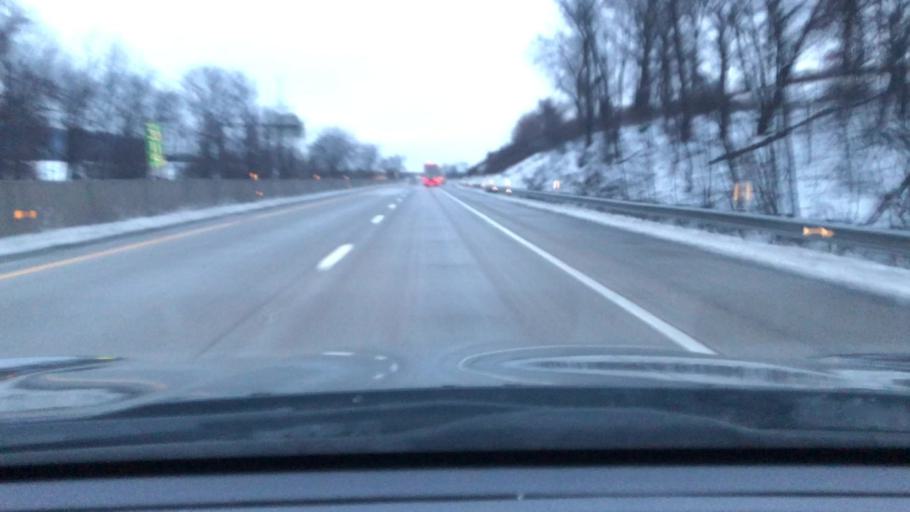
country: US
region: Pennsylvania
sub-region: Berks County
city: Hamburg
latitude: 40.5691
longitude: -75.9651
